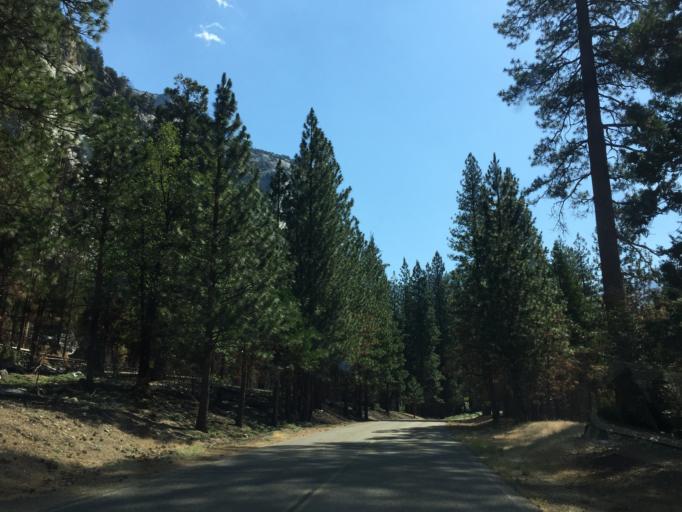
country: US
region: California
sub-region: Tulare County
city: Three Rivers
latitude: 36.7906
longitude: -118.6086
